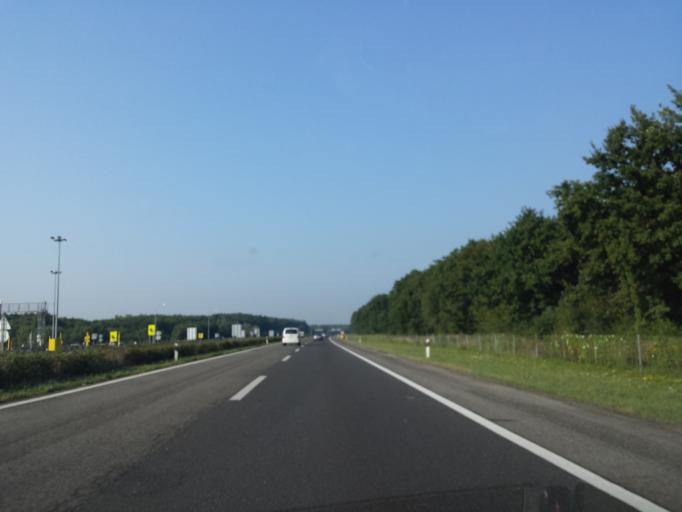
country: HR
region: Grad Zagreb
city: Brezovica
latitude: 45.7235
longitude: 15.8690
